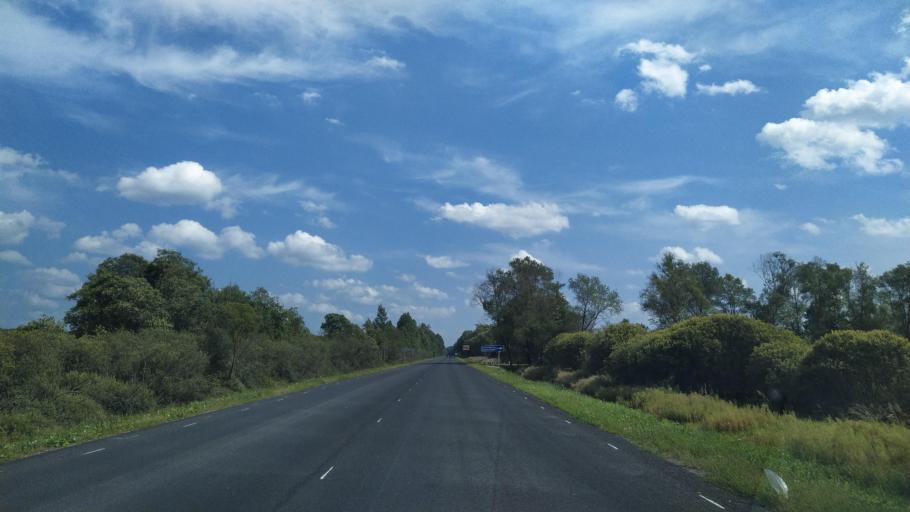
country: RU
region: Pskov
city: Porkhov
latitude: 57.7329
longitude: 29.0883
